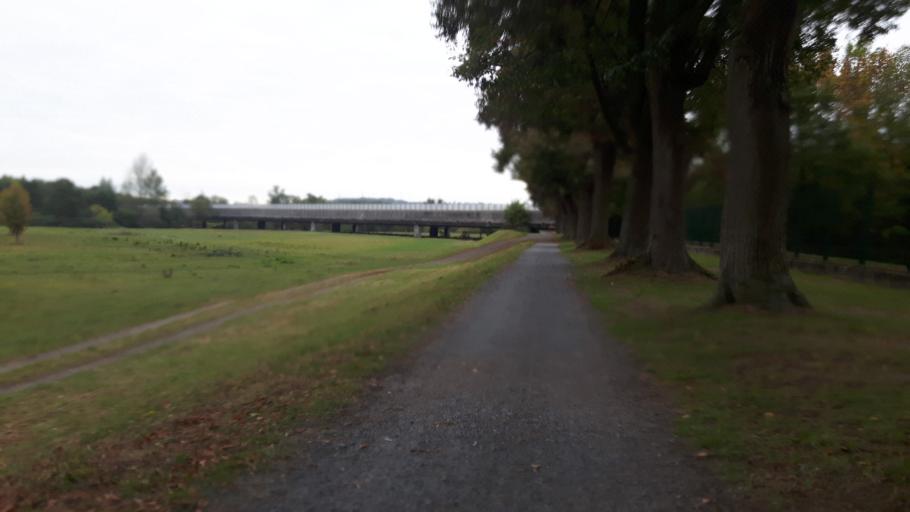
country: DE
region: North Rhine-Westphalia
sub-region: Regierungsbezirk Koln
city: Hennef
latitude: 50.7836
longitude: 7.2860
